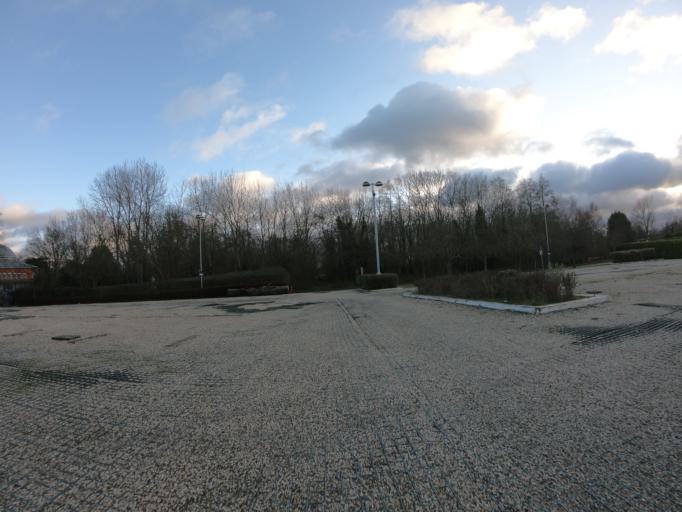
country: GB
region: England
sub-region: Greater London
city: Chislehurst
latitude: 51.4504
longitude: 0.0738
